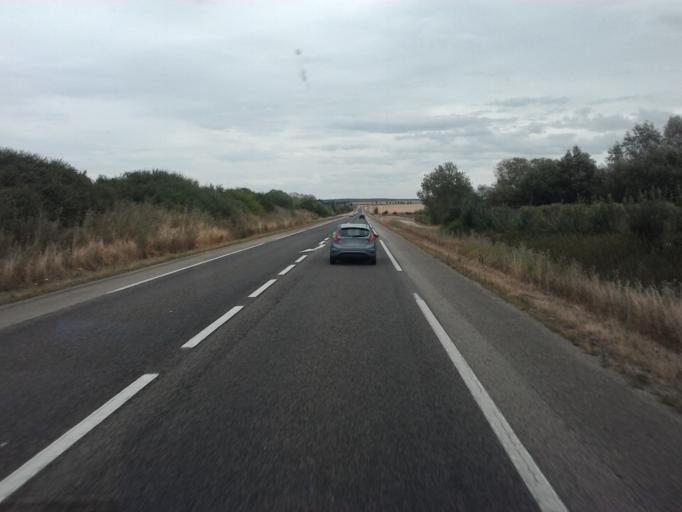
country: FR
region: Lorraine
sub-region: Departement de Meurthe-et-Moselle
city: Bainville-sur-Madon
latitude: 48.5778
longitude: 6.0589
